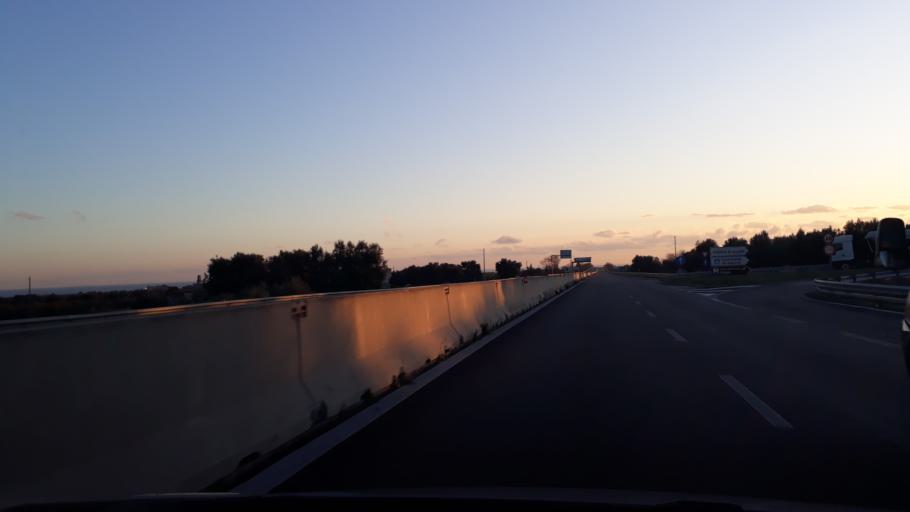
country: IT
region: Apulia
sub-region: Provincia di Brindisi
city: Pezze di Greco
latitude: 40.8341
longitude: 17.4060
